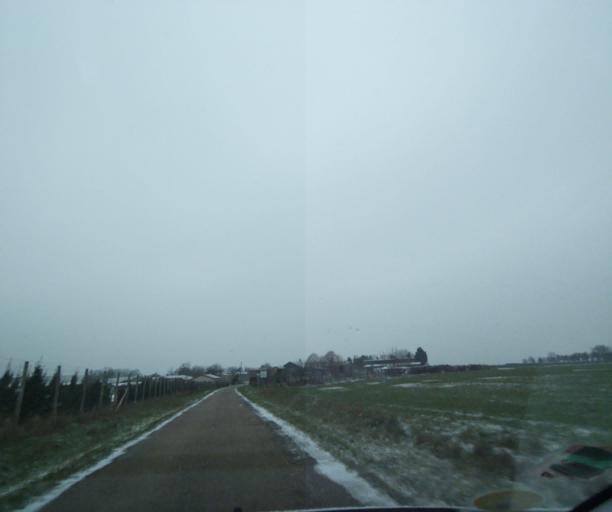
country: FR
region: Champagne-Ardenne
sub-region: Departement de la Haute-Marne
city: Wassy
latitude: 48.4687
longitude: 4.9969
